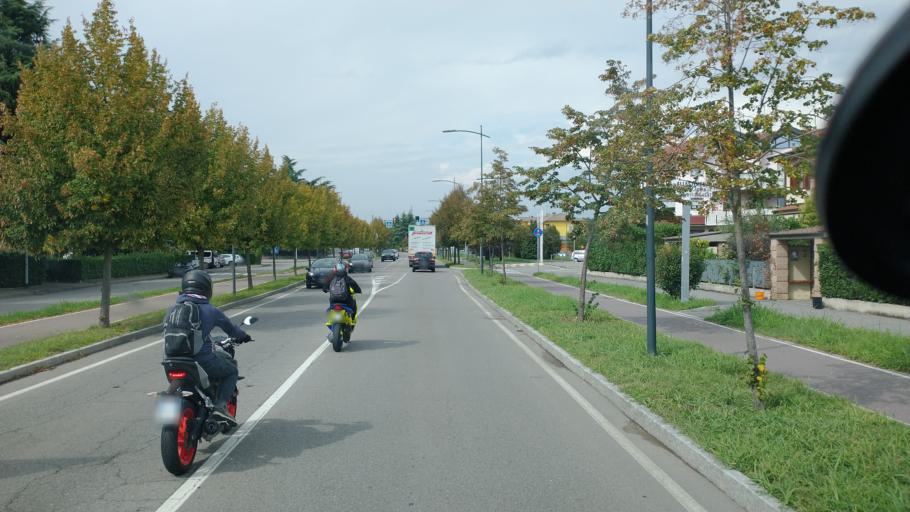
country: IT
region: Lombardy
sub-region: Provincia di Bergamo
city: Treviglio
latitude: 45.5266
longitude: 9.6015
